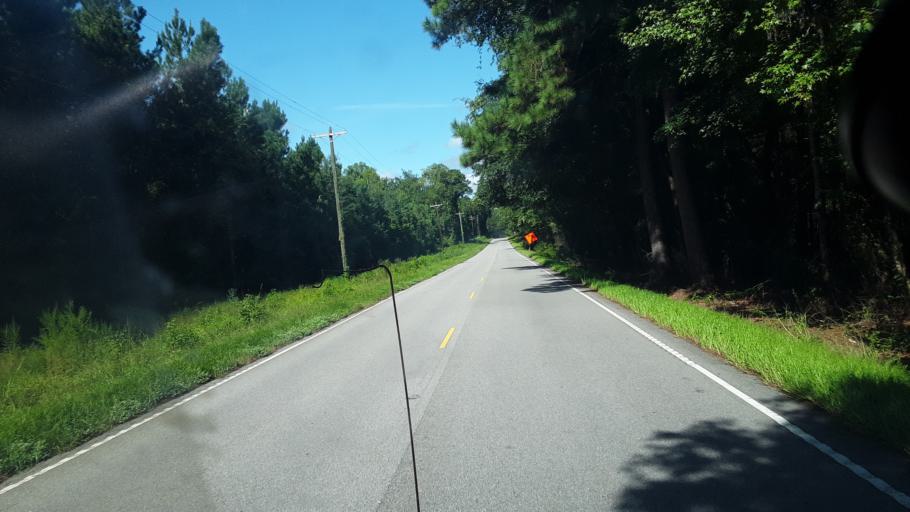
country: US
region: South Carolina
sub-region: Jasper County
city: Ridgeland
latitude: 32.5892
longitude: -80.9417
